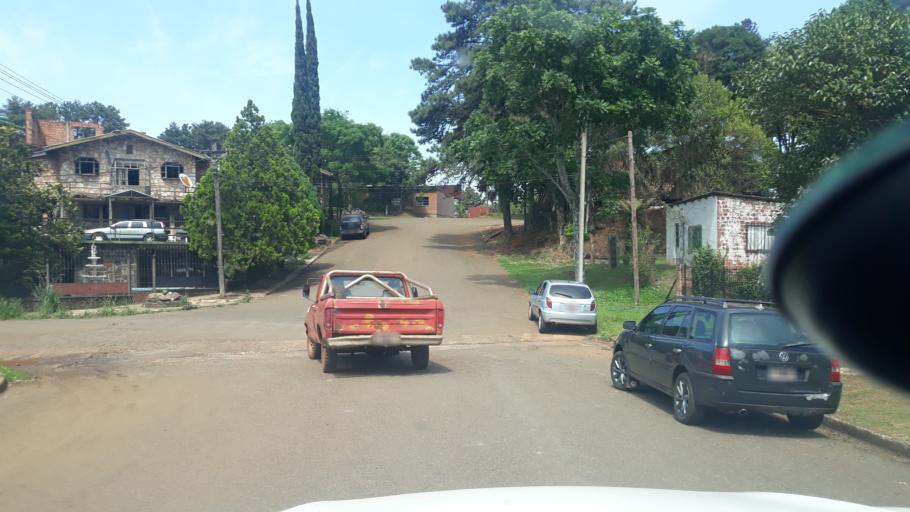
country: AR
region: Misiones
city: Bernardo de Irigoyen
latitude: -26.2529
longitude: -53.6490
